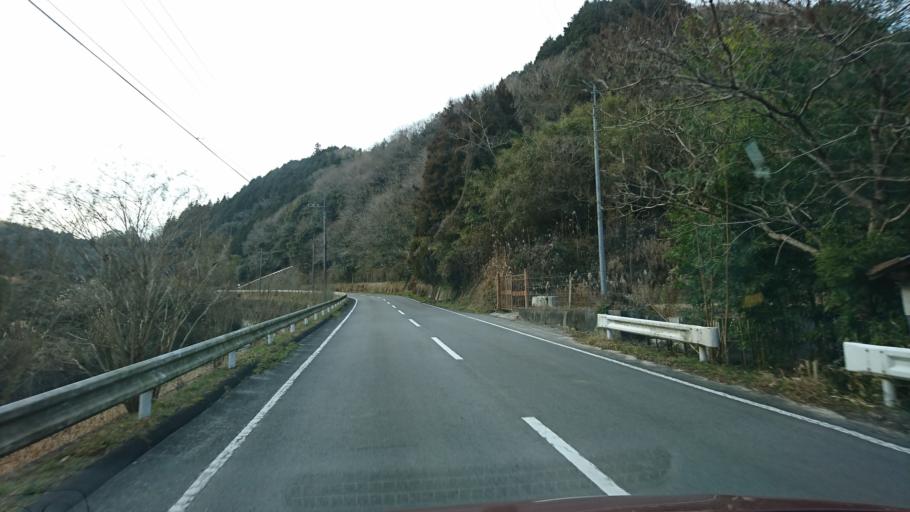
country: JP
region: Ehime
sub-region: Shikoku-chuo Shi
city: Matsuyama
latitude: 33.8989
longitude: 132.8320
